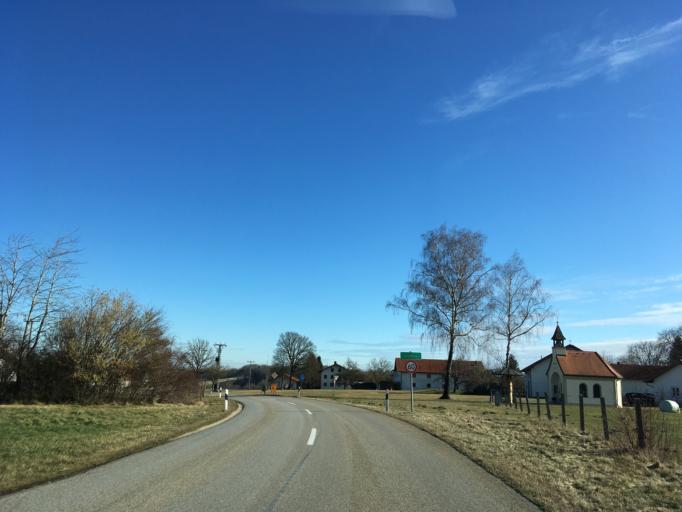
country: DE
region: Bavaria
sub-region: Upper Bavaria
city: Obertaufkirchen
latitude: 48.2422
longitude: 12.2814
